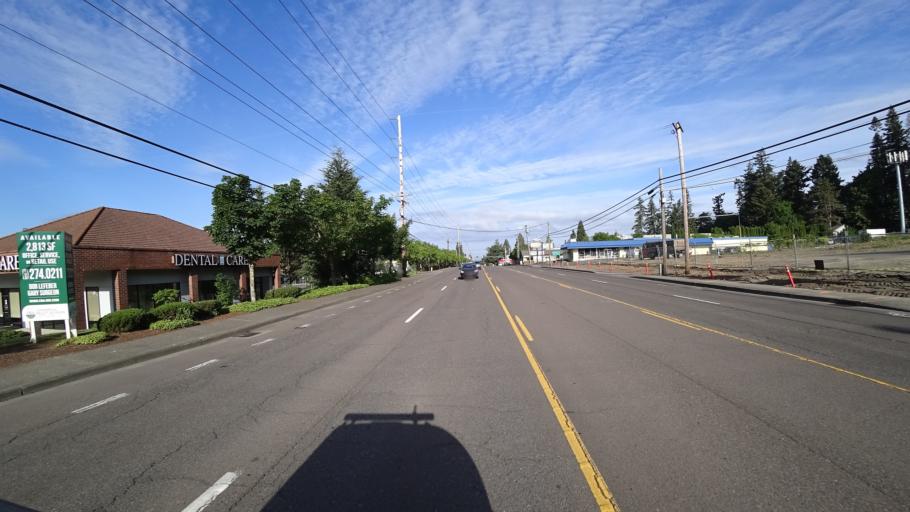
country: US
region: Oregon
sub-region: Washington County
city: Raleigh Hills
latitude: 45.4863
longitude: -122.7652
